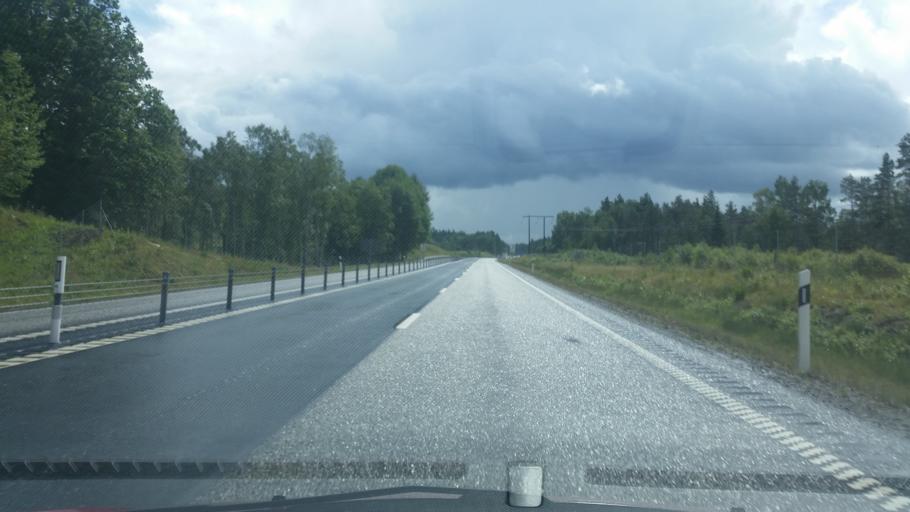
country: SE
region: Joenkoeping
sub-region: Gislaveds Kommun
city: Reftele
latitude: 57.2645
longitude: 13.6298
